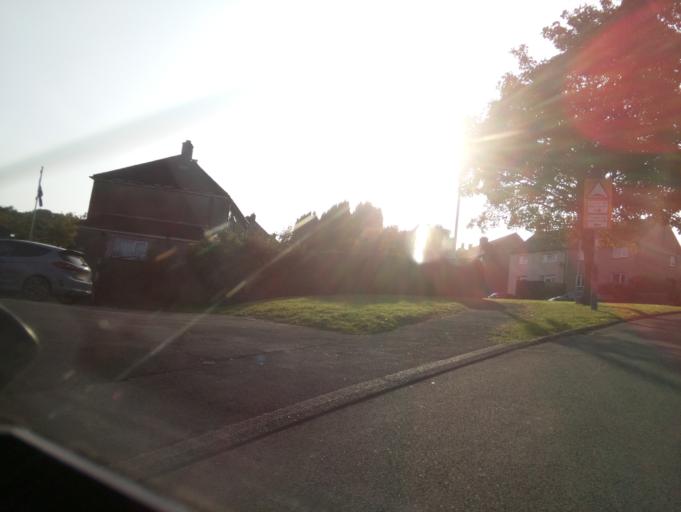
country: GB
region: Wales
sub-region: Torfaen County Borough
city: Pontypool
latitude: 51.6942
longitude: -3.0369
